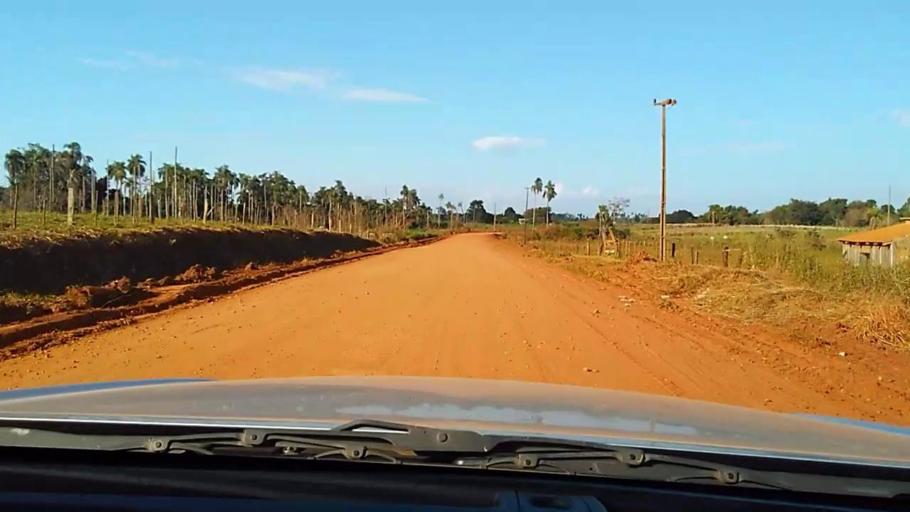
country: PY
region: Alto Parana
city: Doctor Juan Leon Mallorquin
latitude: -25.7040
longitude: -55.3822
